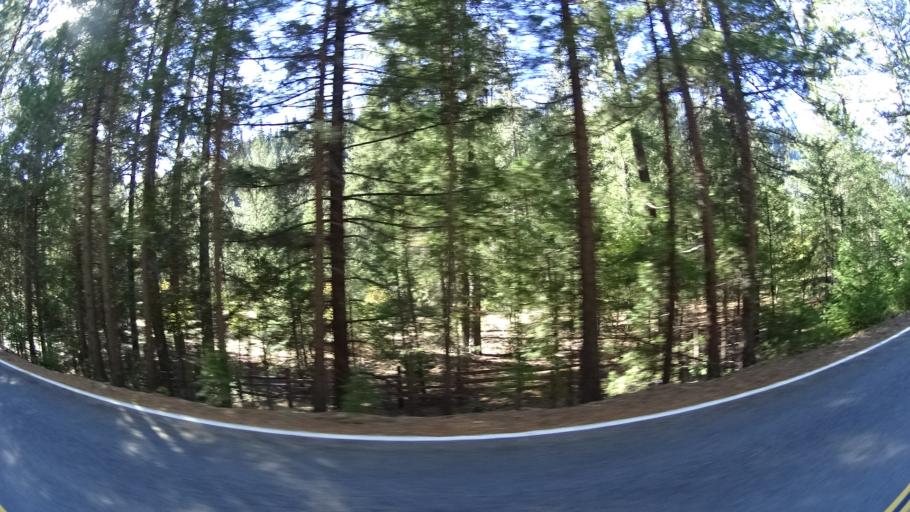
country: US
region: California
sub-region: Trinity County
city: Weaverville
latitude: 41.1413
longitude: -123.1306
